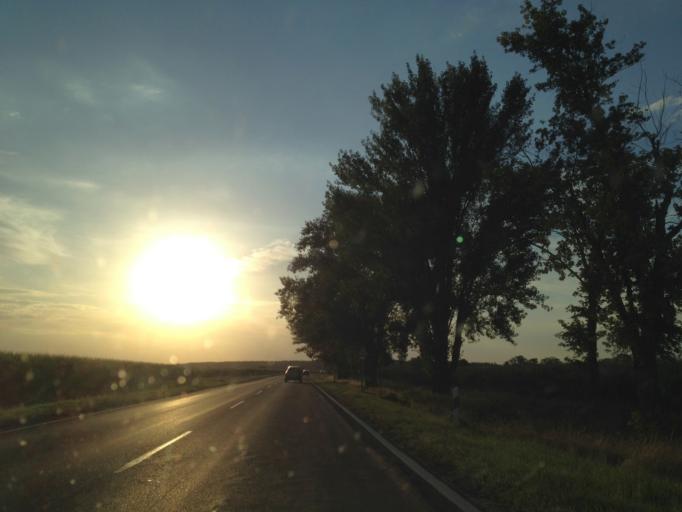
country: HU
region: Gyor-Moson-Sopron
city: Kimle
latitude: 47.8211
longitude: 17.3318
